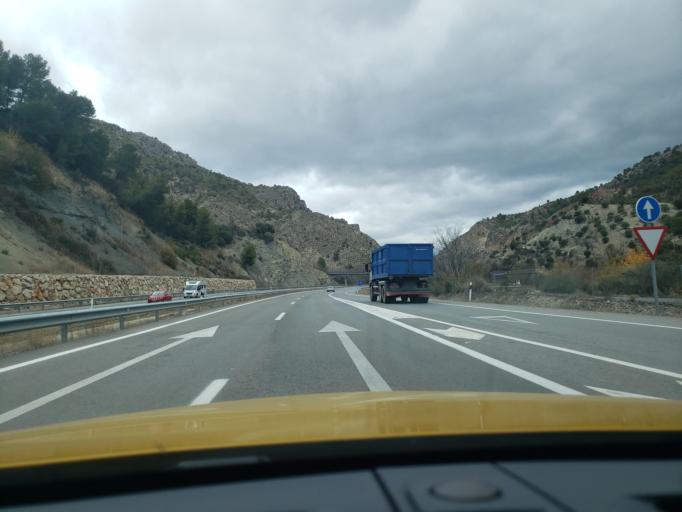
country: ES
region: Andalusia
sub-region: Provincia de Jaen
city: Campillo de Arenas
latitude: 37.5949
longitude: -3.6024
